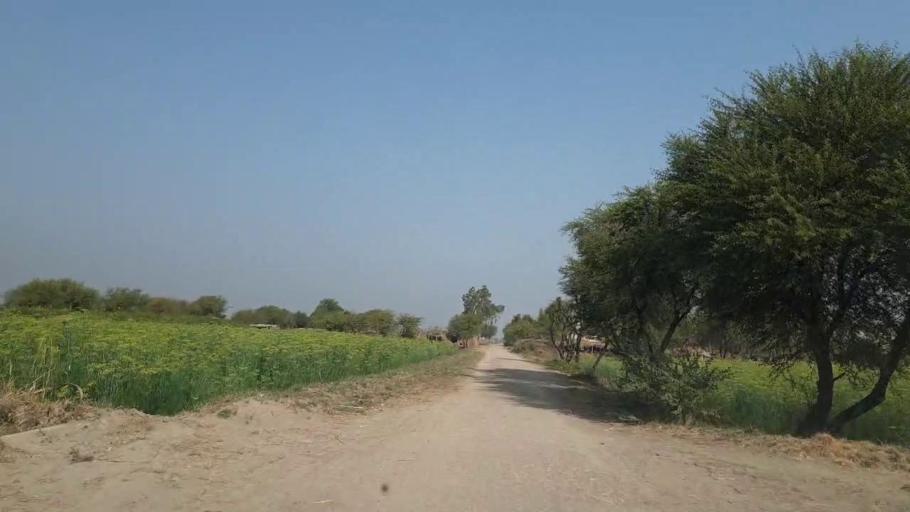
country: PK
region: Sindh
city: Mirpur Khas
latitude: 25.5889
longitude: 69.0149
